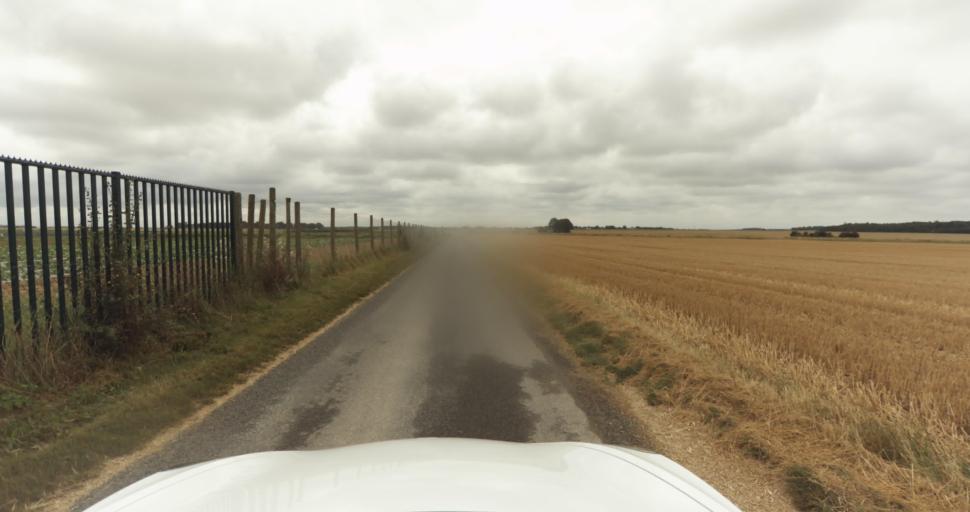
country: FR
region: Haute-Normandie
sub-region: Departement de l'Eure
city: Claville
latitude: 49.0620
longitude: 1.0396
